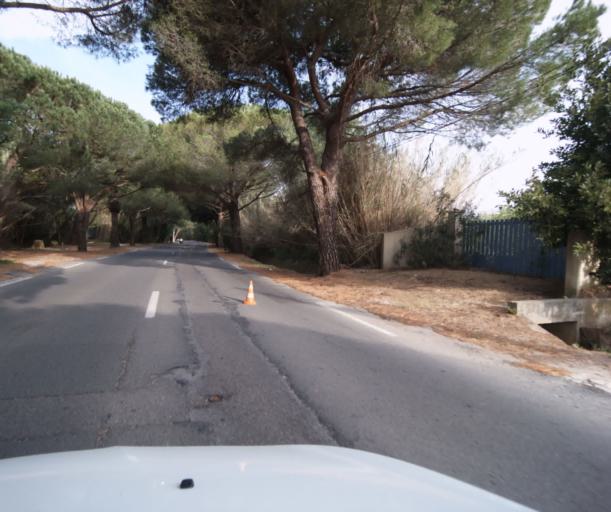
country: FR
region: Provence-Alpes-Cote d'Azur
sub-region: Departement du Var
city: Hyeres
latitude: 43.1131
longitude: 6.1614
